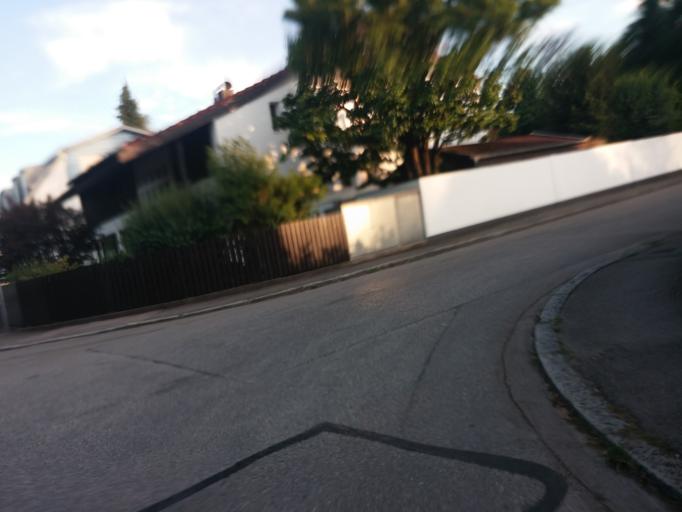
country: DE
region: Bavaria
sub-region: Upper Bavaria
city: Haar
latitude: 48.1061
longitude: 11.6974
